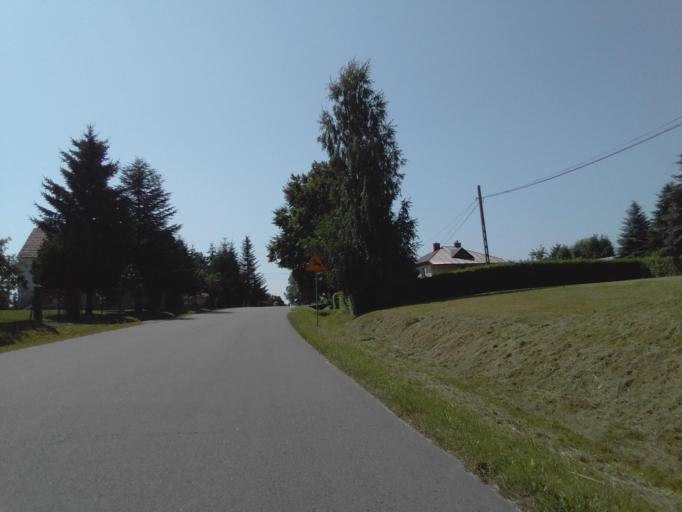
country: PL
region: Subcarpathian Voivodeship
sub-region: Powiat ropczycko-sedziszowski
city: Sedziszow Malopolski
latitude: 50.0661
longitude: 21.6633
